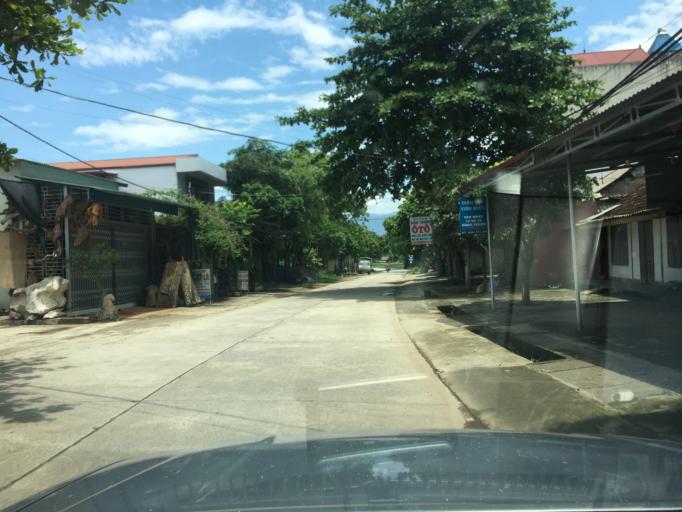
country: VN
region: Yen Bai
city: Son Thinh
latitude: 21.6385
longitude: 104.5026
